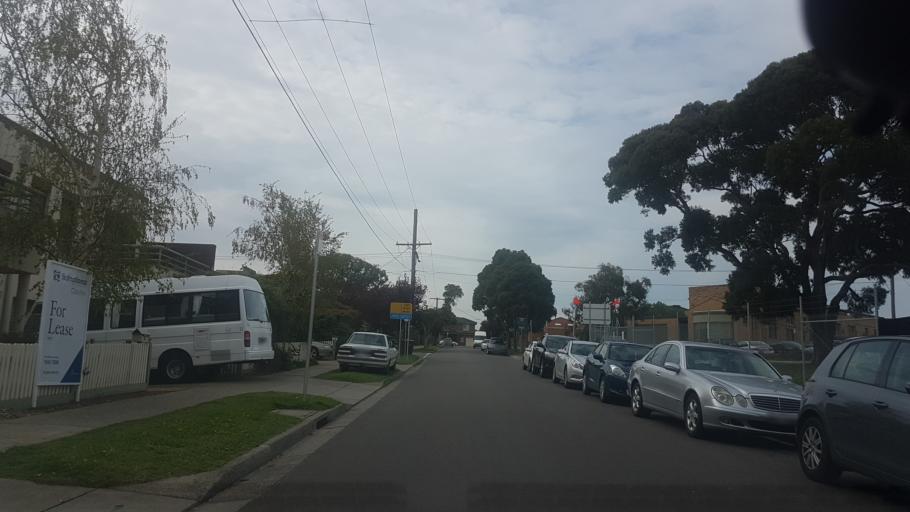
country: AU
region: Victoria
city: Clayton
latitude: -37.9190
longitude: 145.1233
